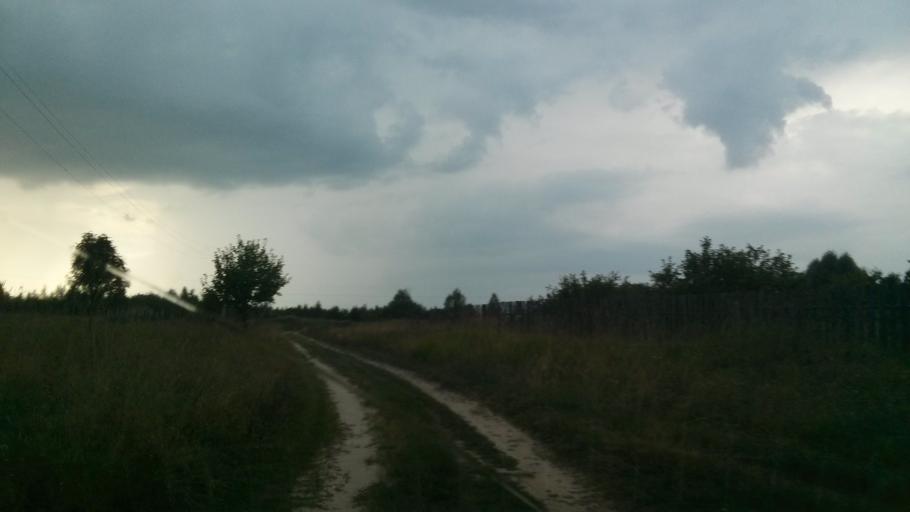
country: RU
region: Nizjnij Novgorod
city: Shimorskoye
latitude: 55.3141
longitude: 41.8648
